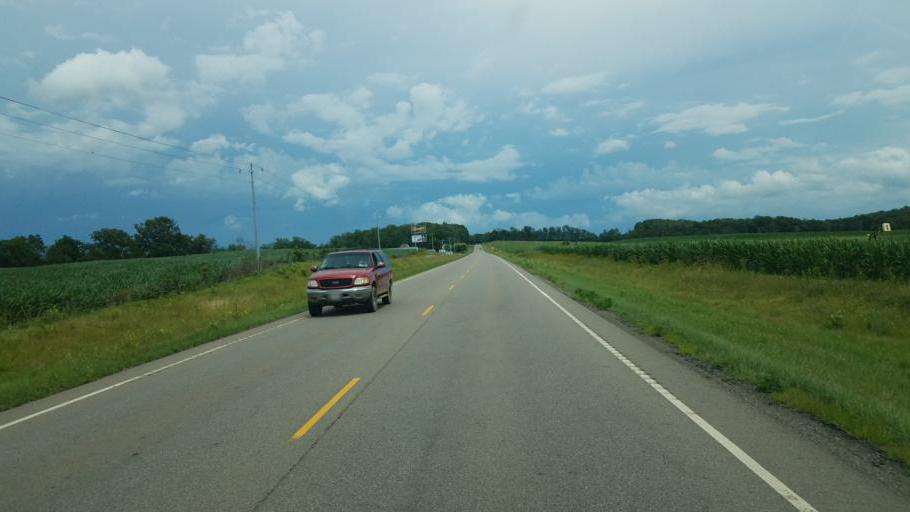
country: US
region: Ohio
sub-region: Licking County
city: Utica
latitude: 40.2314
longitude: -82.4899
